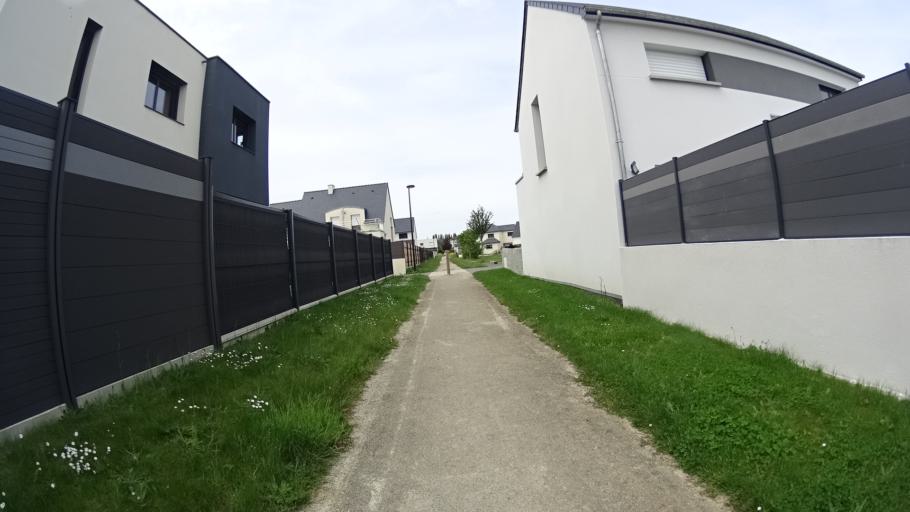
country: FR
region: Brittany
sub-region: Departement d'Ille-et-Vilaine
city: La Meziere
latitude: 48.2118
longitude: -1.7556
